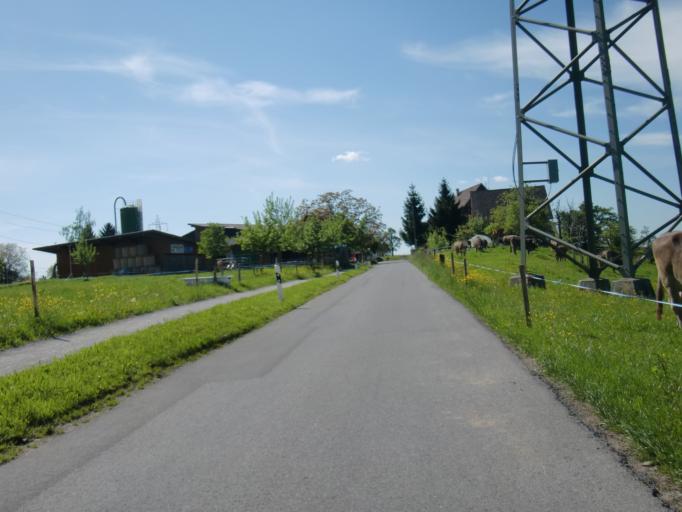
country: CH
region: Zurich
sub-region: Bezirk Hinwil
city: Wolfhausen
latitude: 47.2654
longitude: 8.7988
